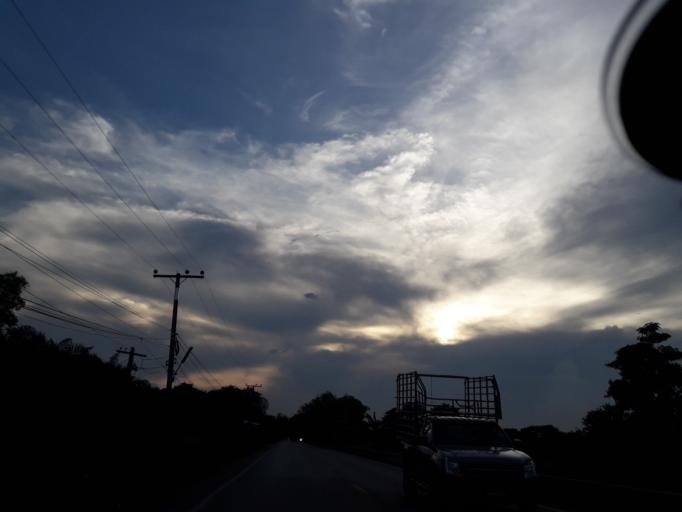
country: TH
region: Sara Buri
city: Nong Khae
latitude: 14.2743
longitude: 100.8883
